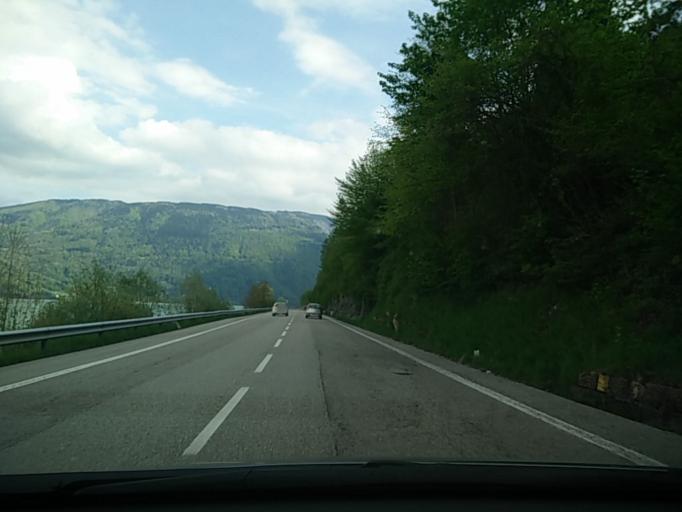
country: IT
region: Veneto
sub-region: Provincia di Belluno
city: Farra d'Alpago
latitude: 46.1238
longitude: 12.3199
